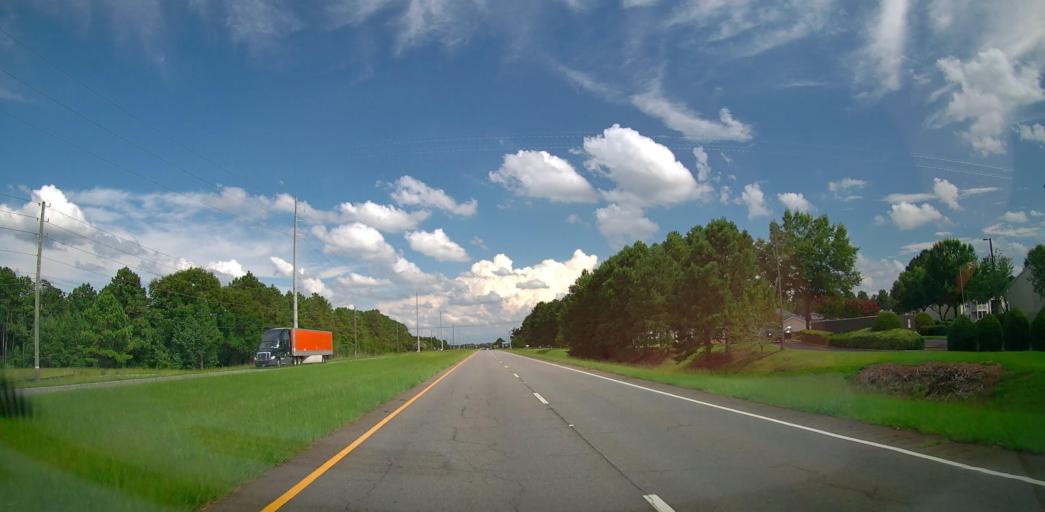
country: US
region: Georgia
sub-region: Houston County
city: Perry
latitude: 32.4801
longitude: -83.7103
